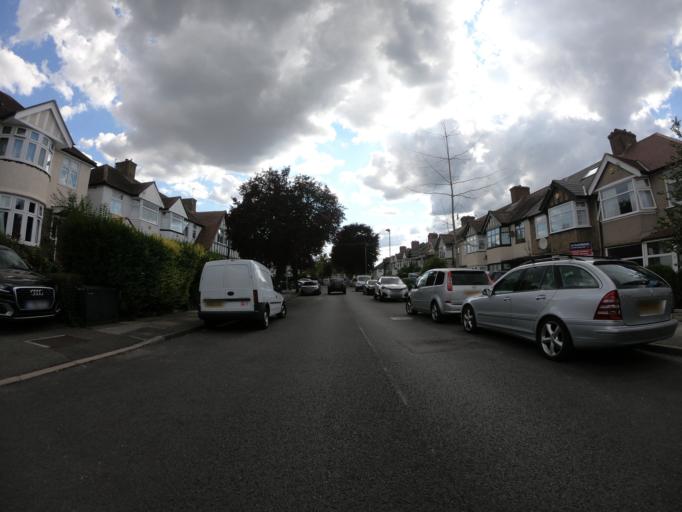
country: GB
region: England
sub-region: Greater London
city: Chislehurst
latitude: 51.4234
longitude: 0.0624
